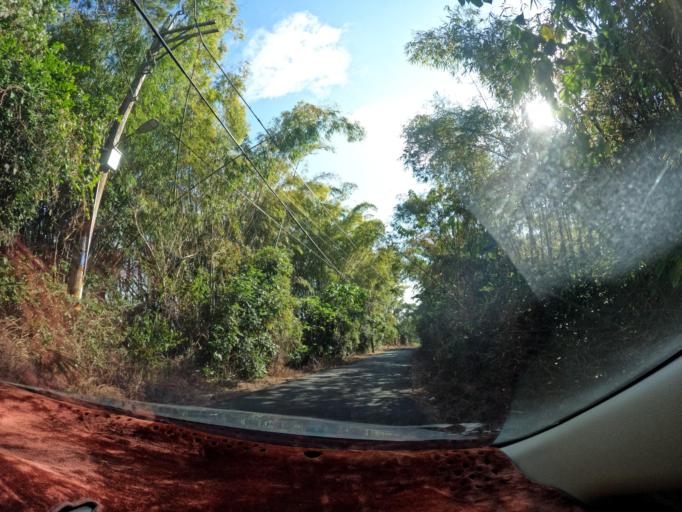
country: TW
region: Taiwan
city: Yujing
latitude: 23.0218
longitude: 120.3843
